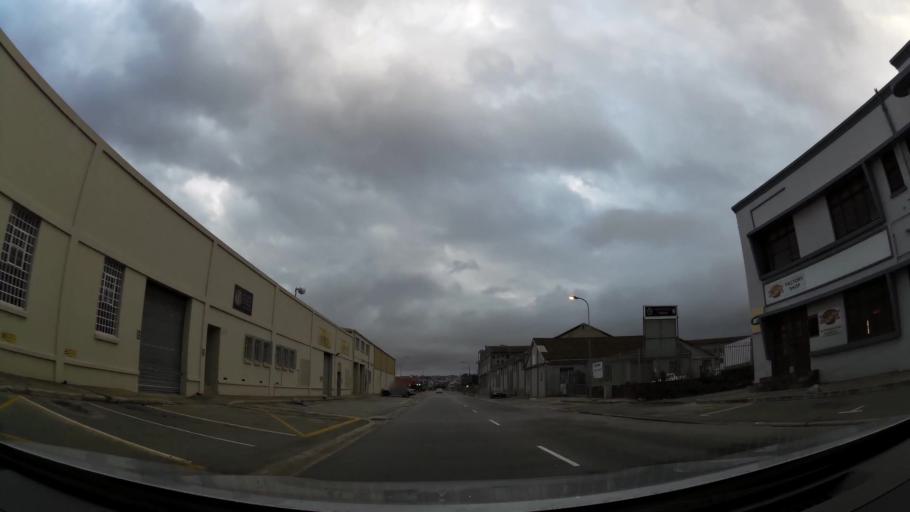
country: ZA
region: Eastern Cape
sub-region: Nelson Mandela Bay Metropolitan Municipality
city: Port Elizabeth
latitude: -33.9364
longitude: 25.6096
